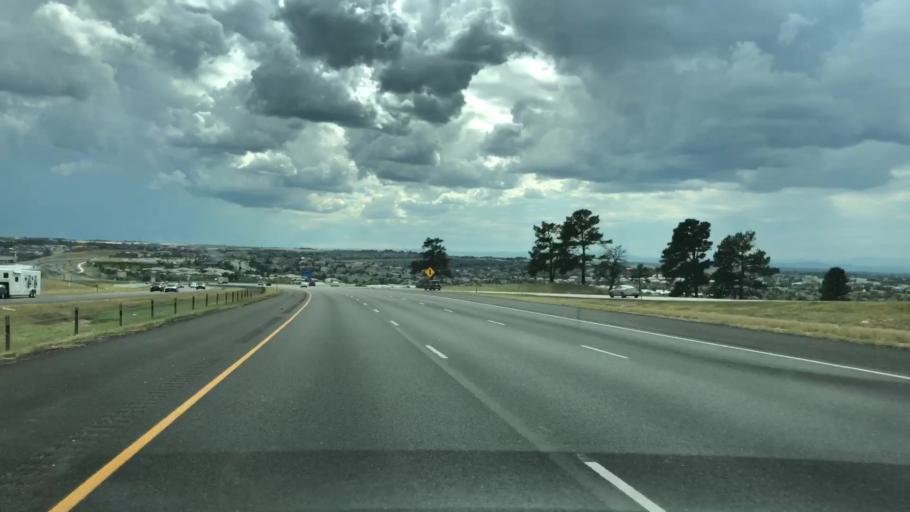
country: US
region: Colorado
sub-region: Douglas County
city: Parker
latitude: 39.5933
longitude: -104.7094
